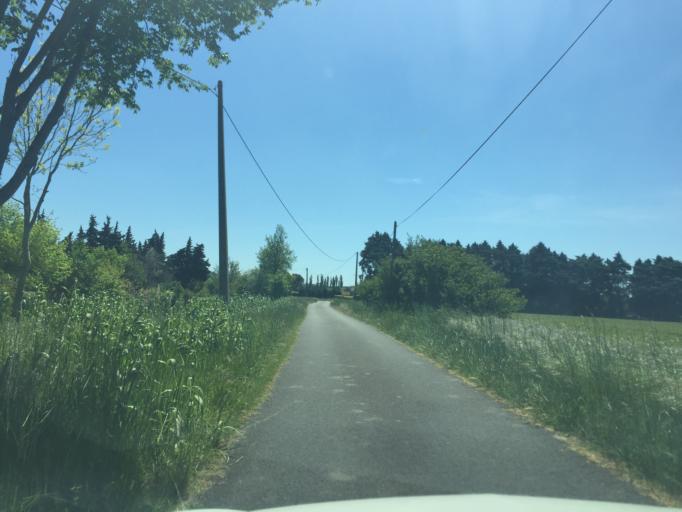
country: FR
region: Provence-Alpes-Cote d'Azur
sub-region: Departement du Vaucluse
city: Caderousse
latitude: 44.1081
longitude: 4.7859
